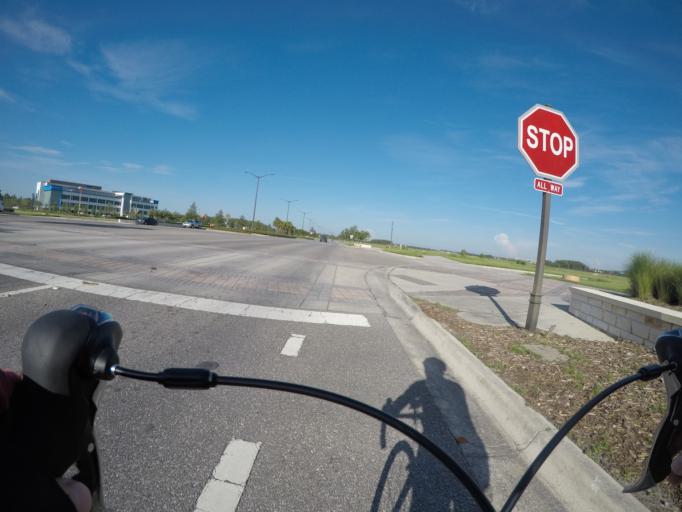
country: US
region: Florida
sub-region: Osceola County
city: Buenaventura Lakes
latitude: 28.3689
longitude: -81.2894
